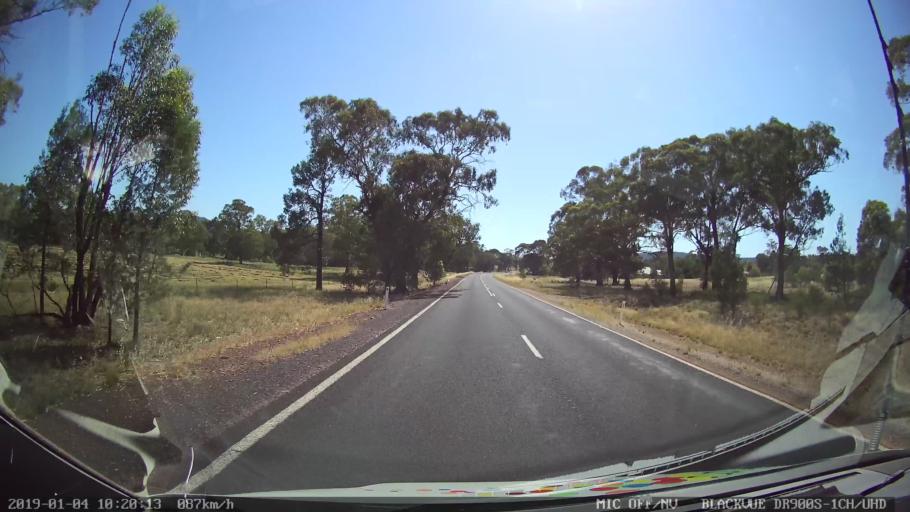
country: AU
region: New South Wales
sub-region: Cabonne
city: Canowindra
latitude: -33.3729
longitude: 148.4923
